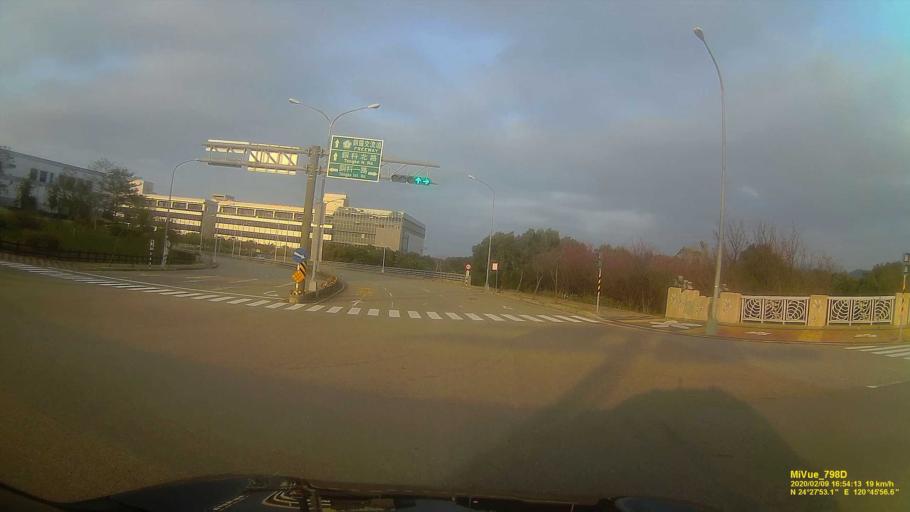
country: TW
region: Taiwan
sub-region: Miaoli
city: Miaoli
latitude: 24.4651
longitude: 120.7660
